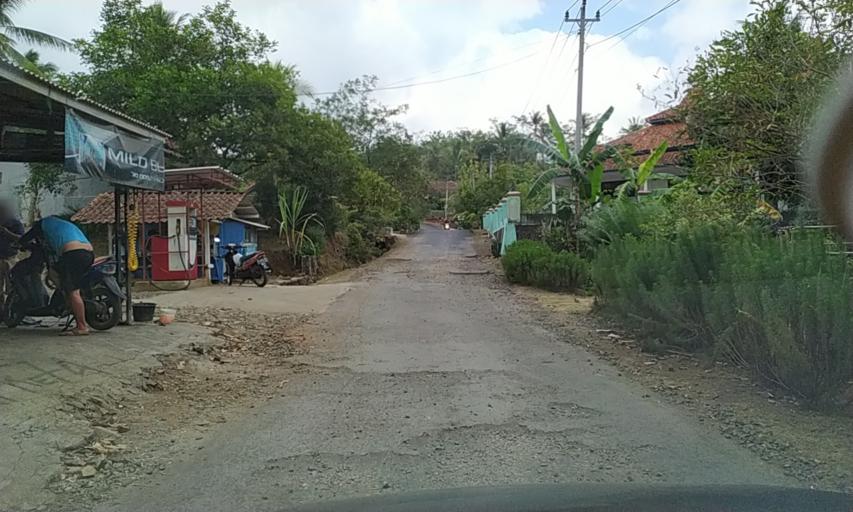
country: ID
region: Central Java
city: Ciwalen
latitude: -7.2876
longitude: 108.6185
